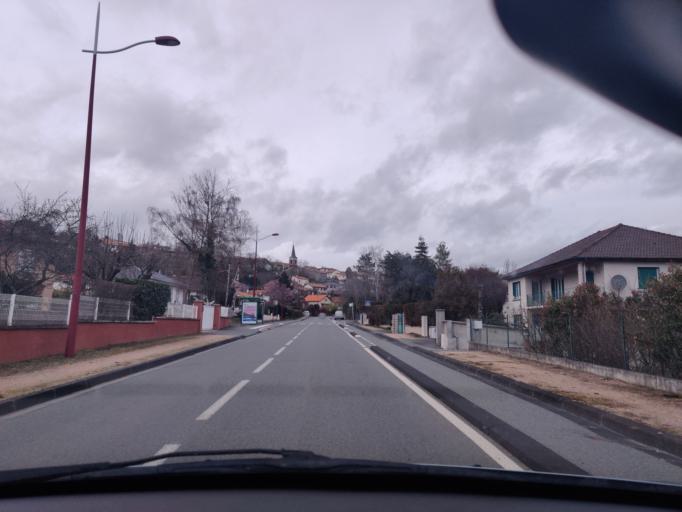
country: FR
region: Auvergne
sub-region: Departement du Puy-de-Dome
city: Enval
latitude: 45.9070
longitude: 3.0569
